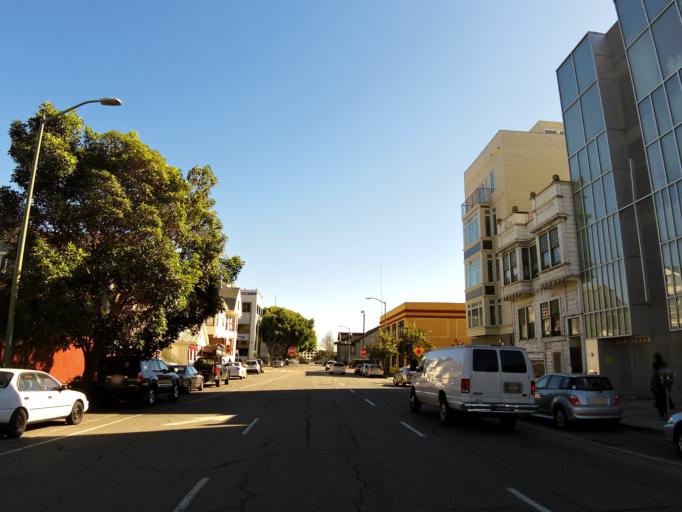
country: US
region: California
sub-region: Alameda County
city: Oakland
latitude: 37.7994
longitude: -122.2696
